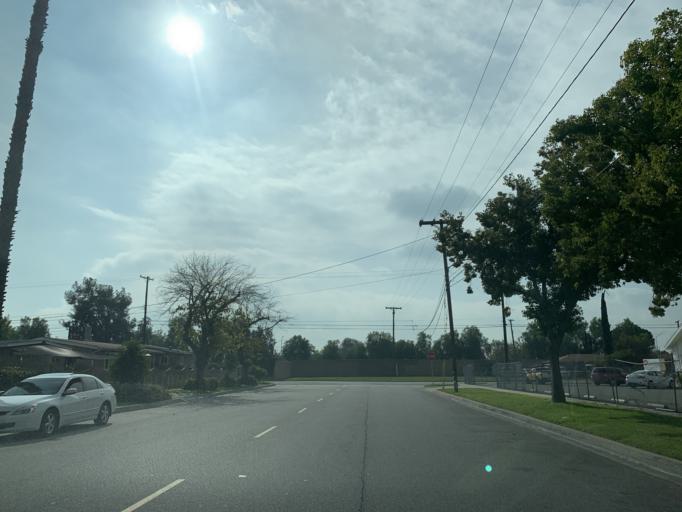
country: US
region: California
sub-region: Los Angeles County
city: Azusa
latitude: 34.1223
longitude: -117.9025
